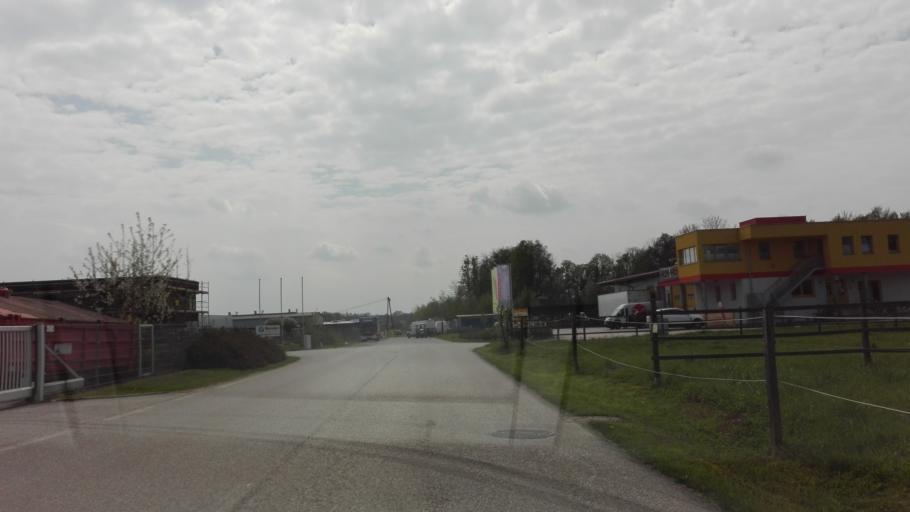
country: AT
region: Upper Austria
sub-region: Politischer Bezirk Perg
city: Perg
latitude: 48.2269
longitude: 14.6990
